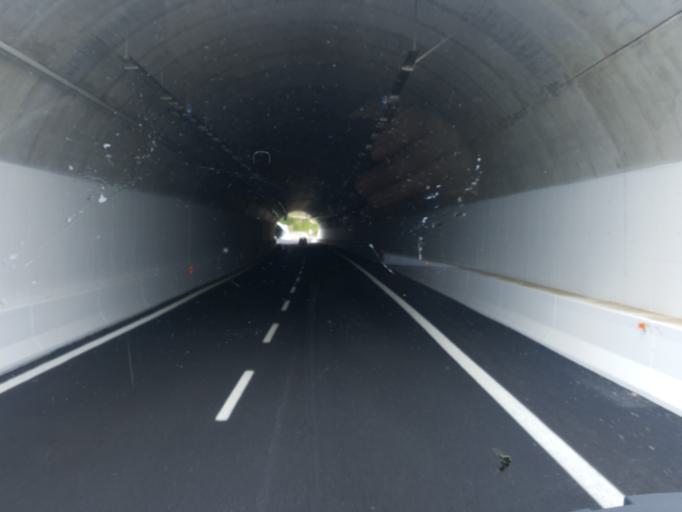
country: IT
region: Latium
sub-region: Provincia di Viterbo
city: Monte Romano
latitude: 42.2838
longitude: 11.9319
